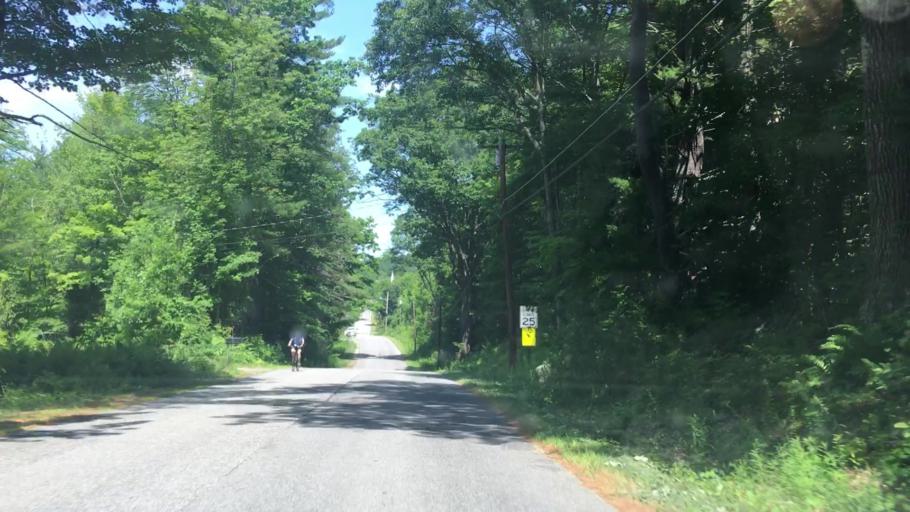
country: US
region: Maine
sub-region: Kennebec County
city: Wayne
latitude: 44.3428
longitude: -70.0618
